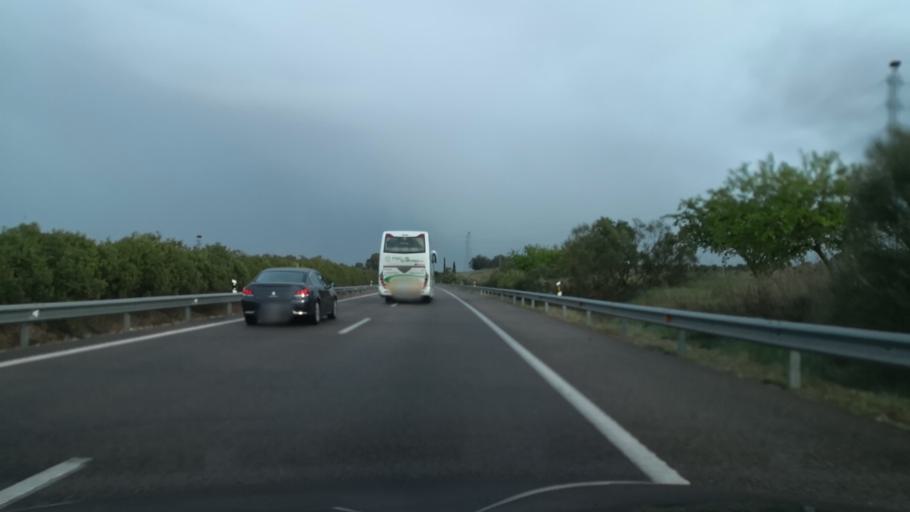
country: ES
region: Extremadura
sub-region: Provincia de Badajoz
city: Badajoz
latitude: 38.8769
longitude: -6.8823
